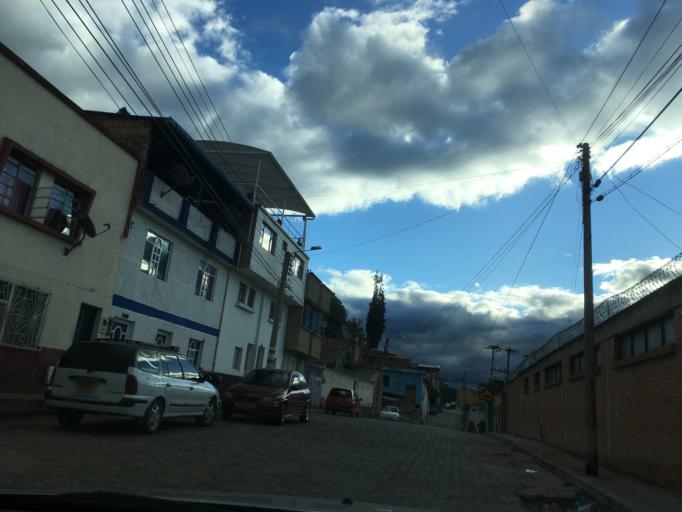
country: CO
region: Boyaca
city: Sogamoso
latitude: 5.7151
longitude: -72.9242
